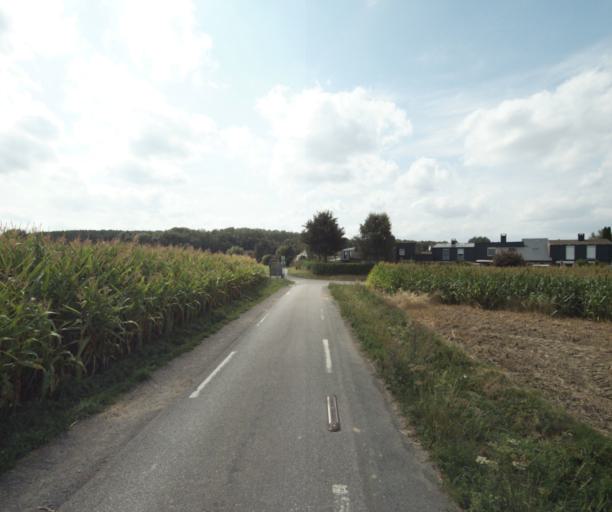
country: FR
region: Nord-Pas-de-Calais
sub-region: Departement du Nord
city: Hem
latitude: 50.6425
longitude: 3.1684
